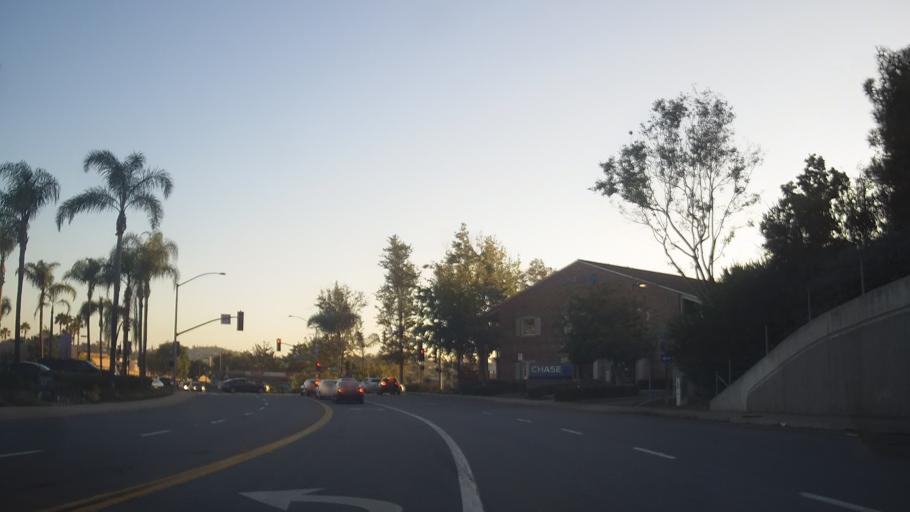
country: US
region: California
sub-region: San Diego County
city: La Mesa
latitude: 32.7793
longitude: -117.0064
